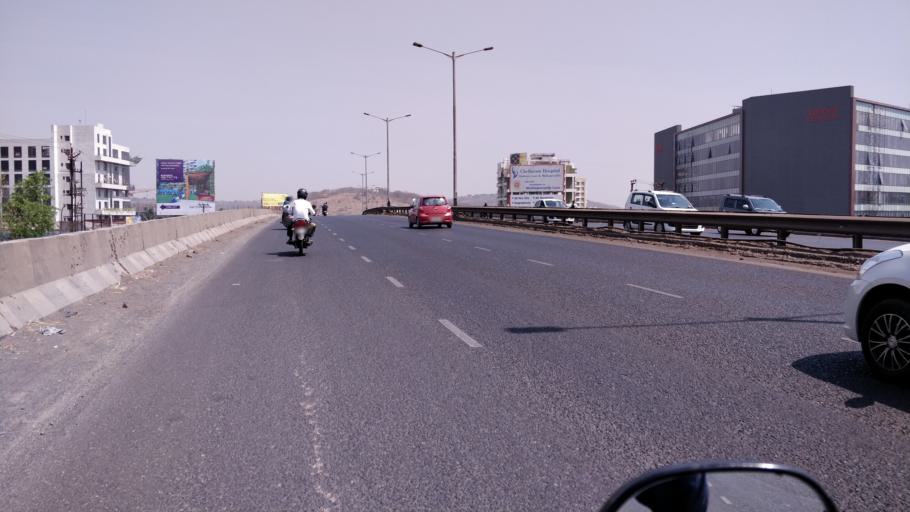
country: IN
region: Maharashtra
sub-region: Pune Division
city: Kharakvasla
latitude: 18.5184
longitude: 73.7688
